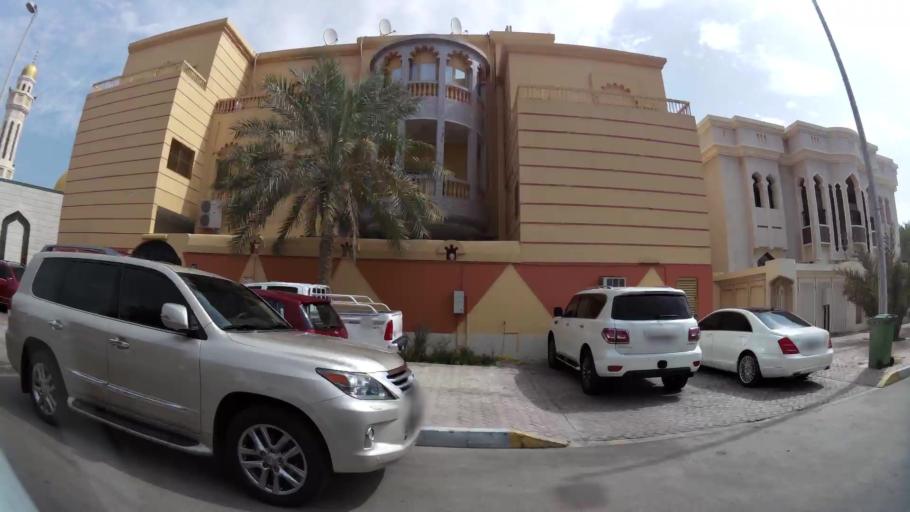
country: AE
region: Abu Dhabi
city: Abu Dhabi
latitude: 24.4646
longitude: 54.3597
